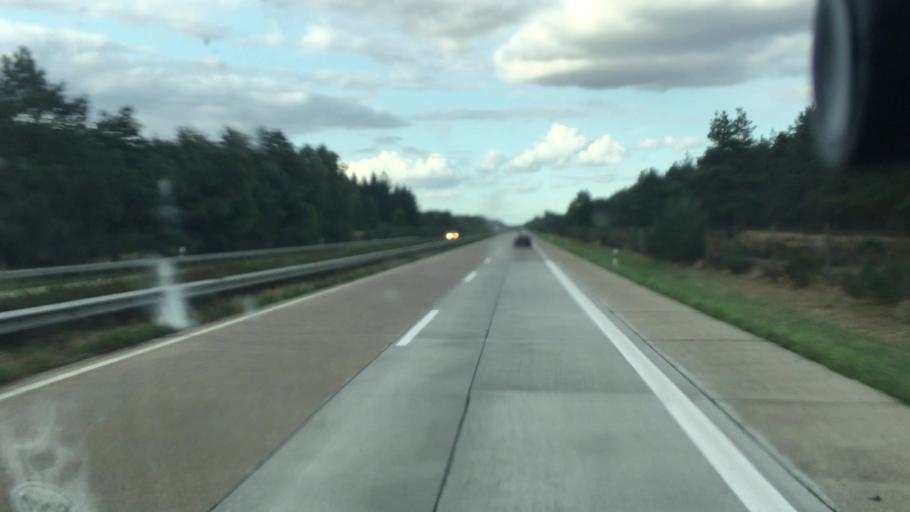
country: DE
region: Lower Saxony
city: Emstek
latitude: 52.9164
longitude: 8.1675
